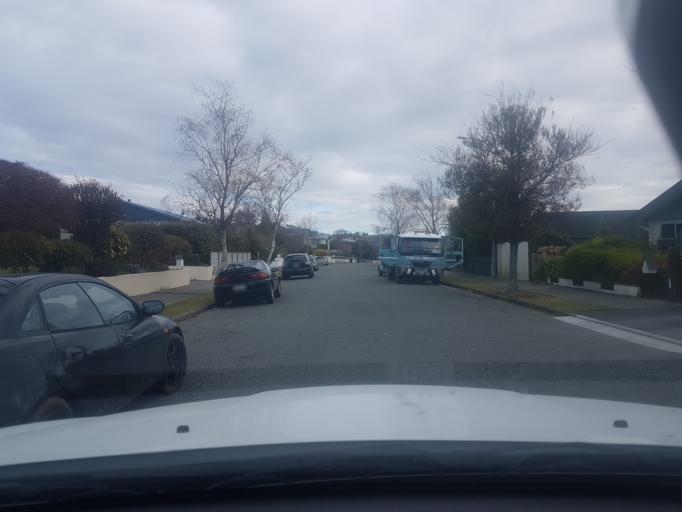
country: NZ
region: Canterbury
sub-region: Timaru District
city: Timaru
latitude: -44.3902
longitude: 171.2085
